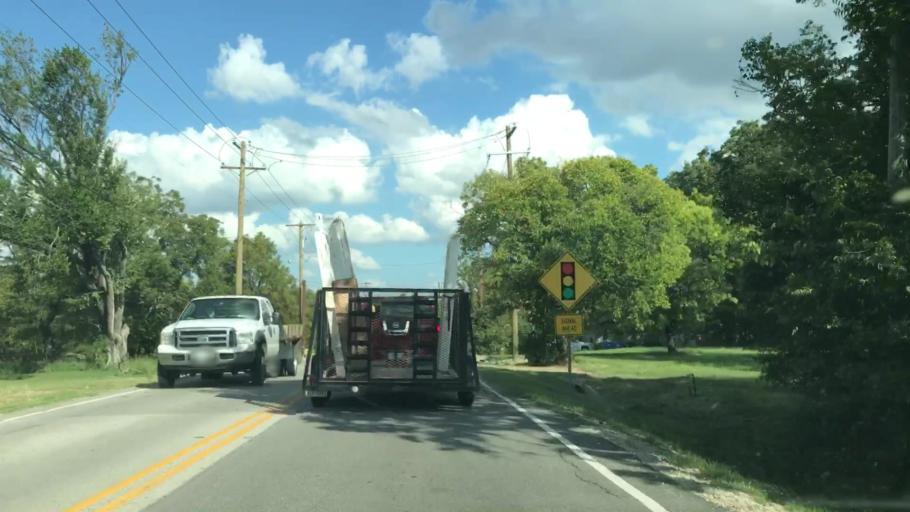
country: US
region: Texas
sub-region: Dallas County
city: Rowlett
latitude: 32.8810
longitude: -96.5205
